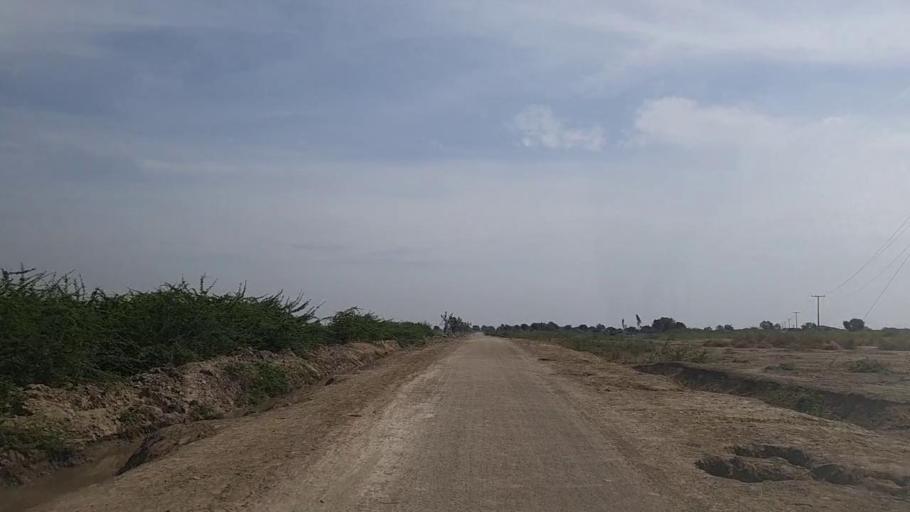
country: PK
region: Sindh
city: Samaro
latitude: 25.2041
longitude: 69.4616
